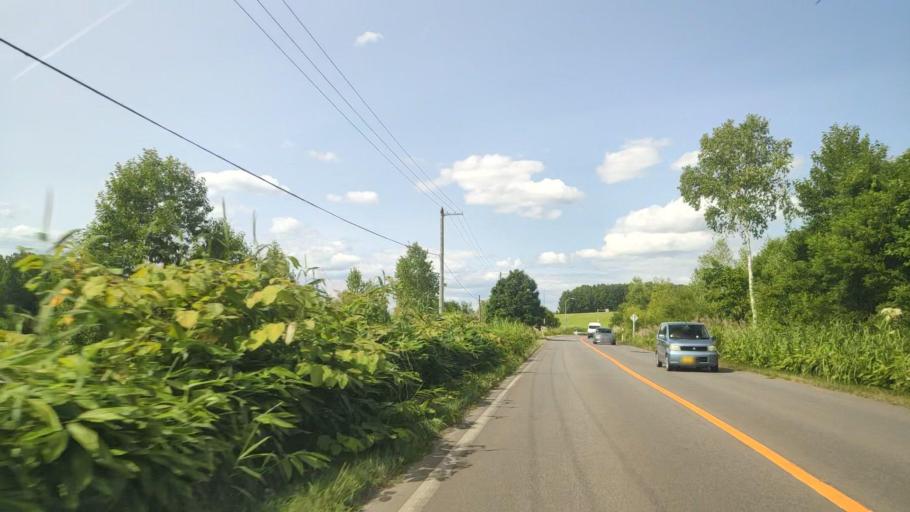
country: JP
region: Hokkaido
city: Nayoro
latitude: 44.2769
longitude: 142.4231
